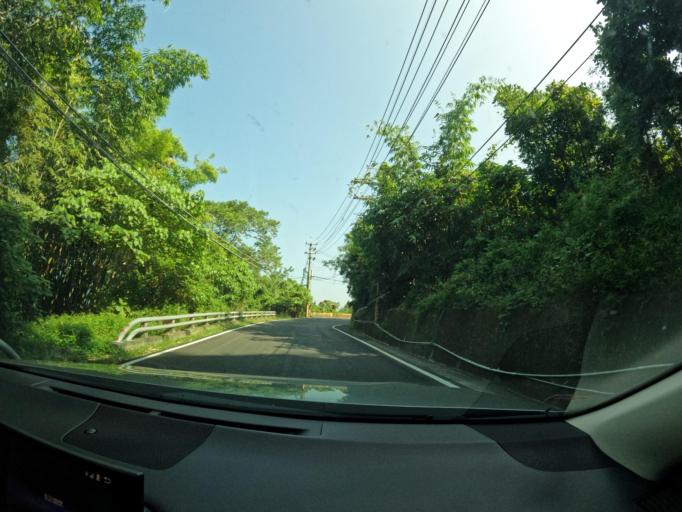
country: TW
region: Taiwan
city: Yujing
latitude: 23.0749
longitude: 120.6107
